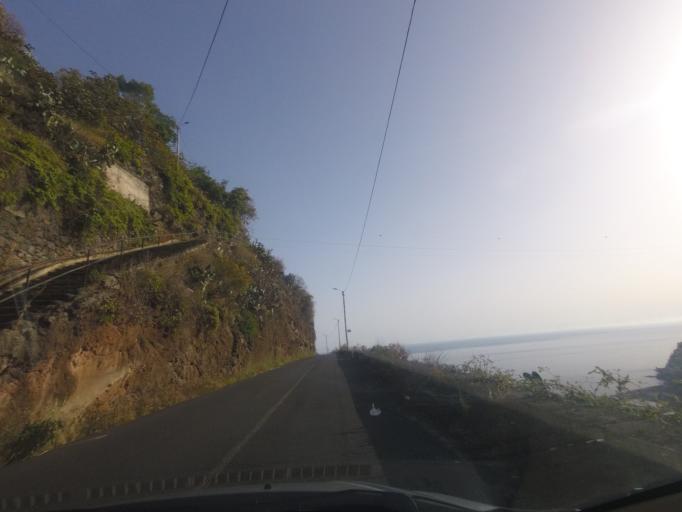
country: PT
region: Madeira
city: Ponta do Sol
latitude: 32.6846
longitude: -17.0827
